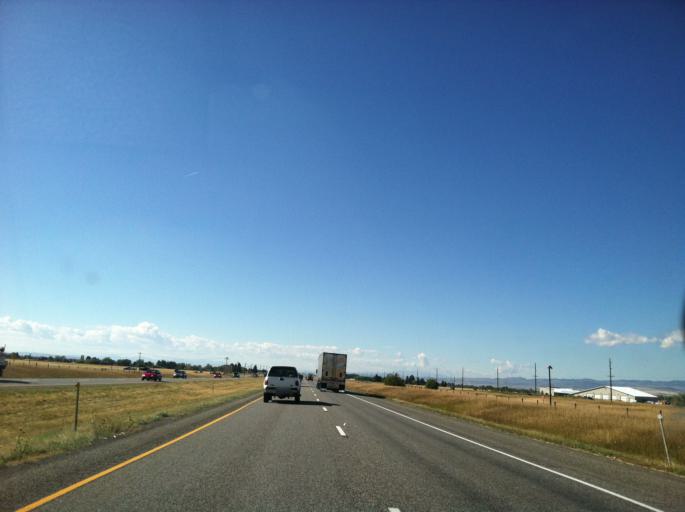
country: US
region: Montana
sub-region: Gallatin County
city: Bozeman
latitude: 45.7237
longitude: -111.0783
